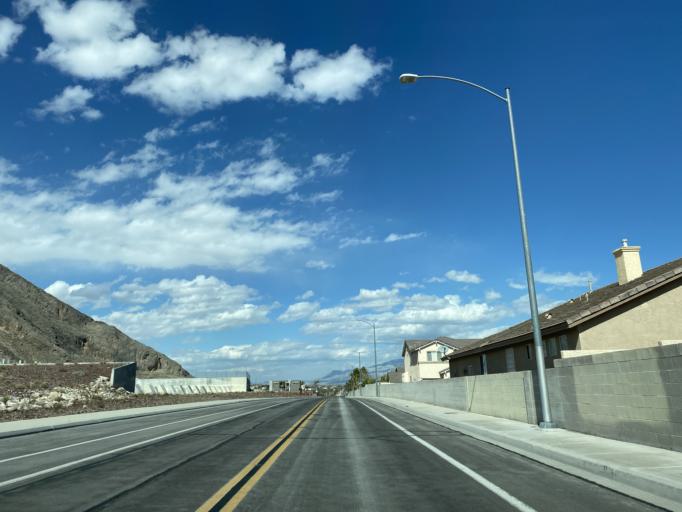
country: US
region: Nevada
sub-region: Clark County
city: Summerlin South
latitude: 36.2305
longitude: -115.3086
